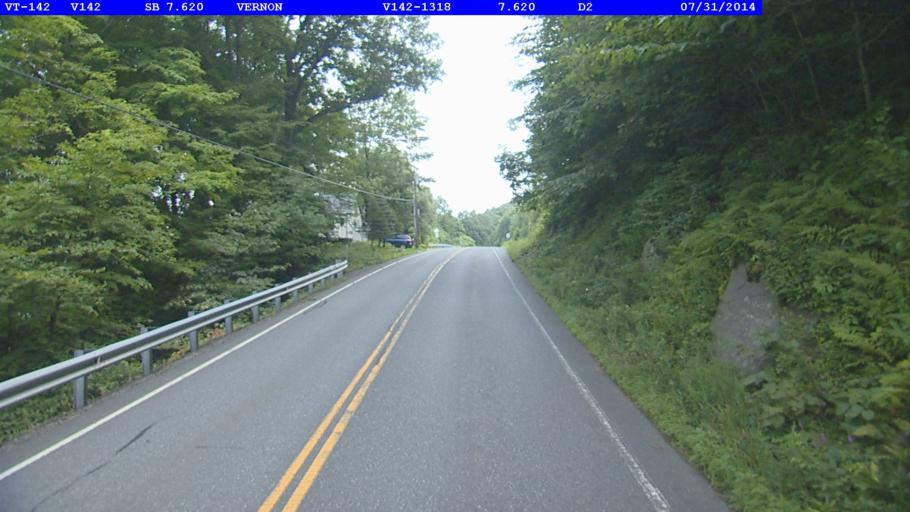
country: US
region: Vermont
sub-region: Windham County
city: Brattleboro
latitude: 42.8102
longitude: -72.5443
